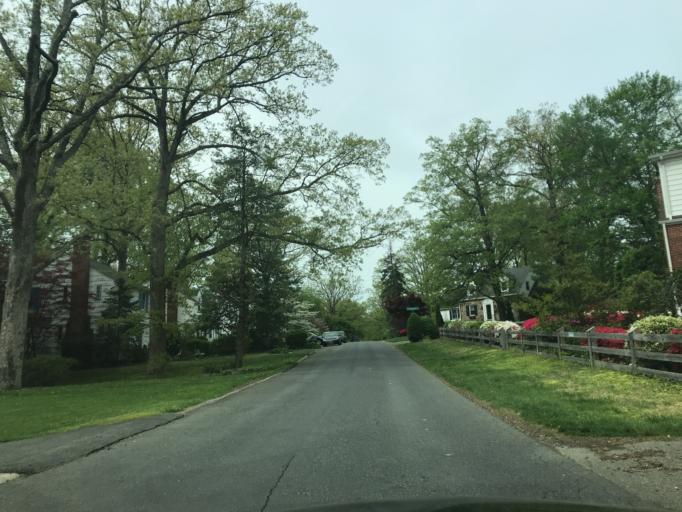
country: US
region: Maryland
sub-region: Baltimore County
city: Catonsville
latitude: 39.2607
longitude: -76.7438
